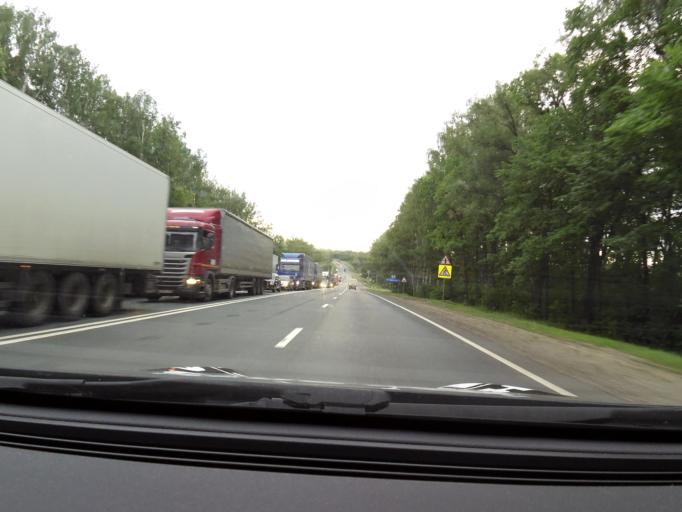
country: RU
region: Chuvashia
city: Tsivil'sk
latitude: 55.9001
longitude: 47.4308
